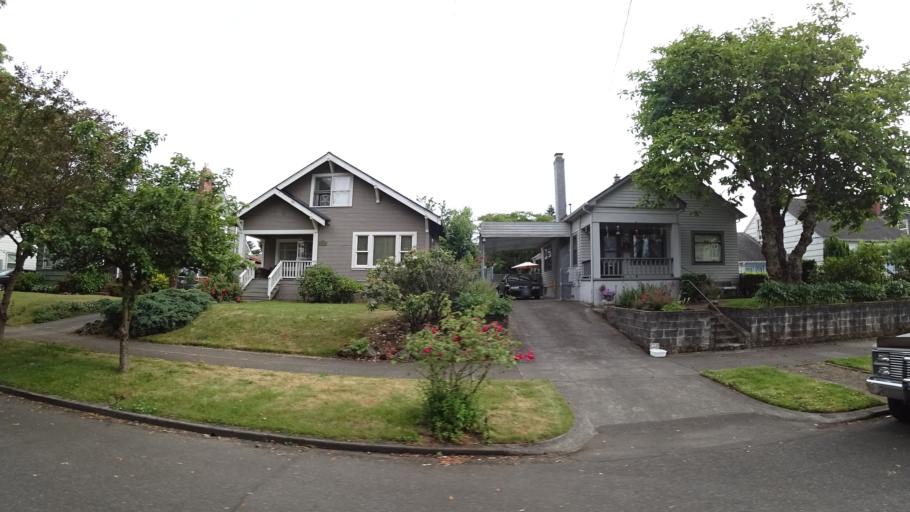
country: US
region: Oregon
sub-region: Multnomah County
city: Portland
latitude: 45.5613
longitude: -122.6910
